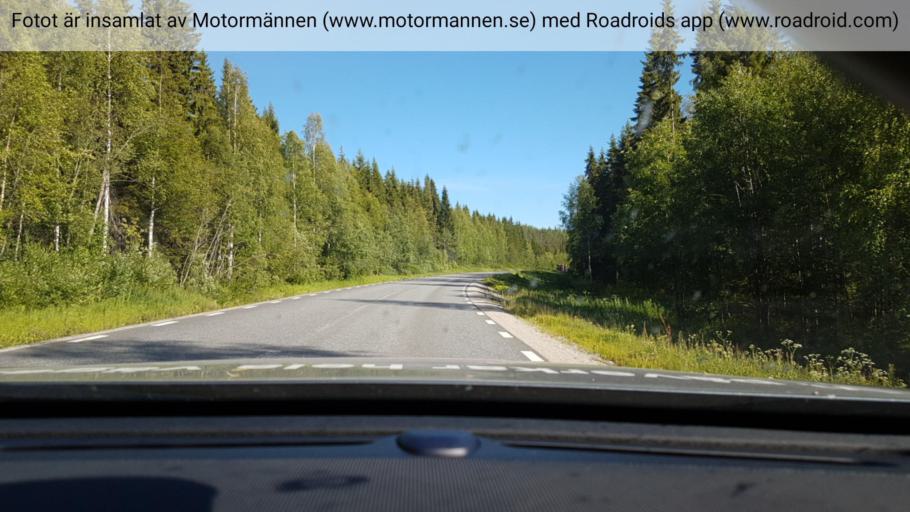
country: SE
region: Vaesterbotten
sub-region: Bjurholms Kommun
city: Bjurholm
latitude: 64.3794
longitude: 19.1342
